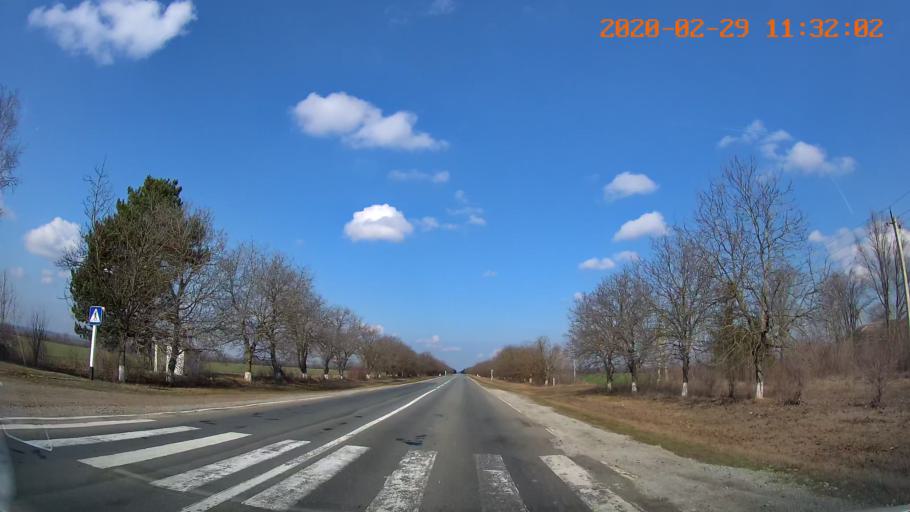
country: MD
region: Rezina
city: Saharna
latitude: 47.5321
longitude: 29.0987
